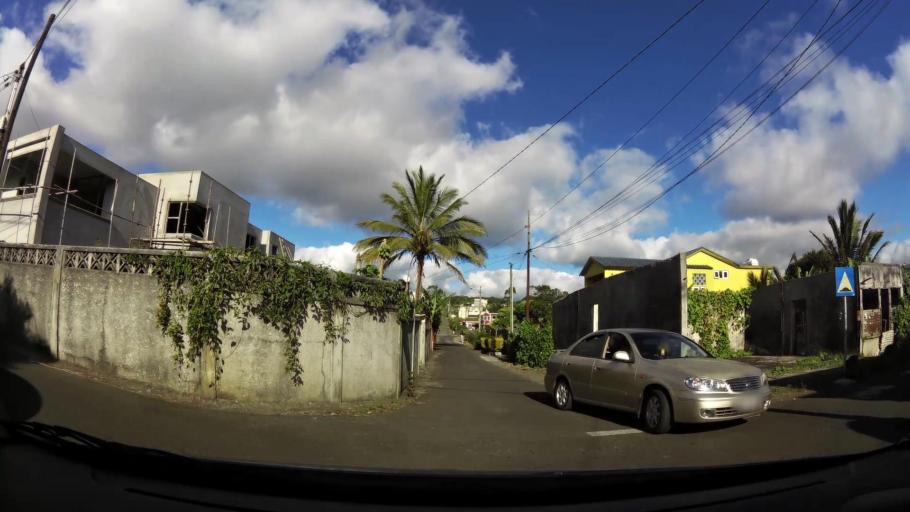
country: MU
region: Plaines Wilhems
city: Curepipe
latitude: -20.2913
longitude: 57.5204
